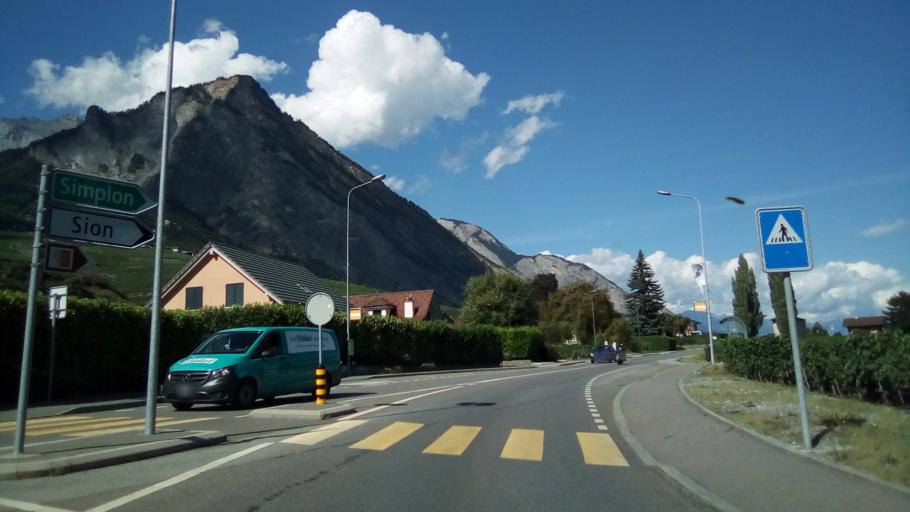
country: CH
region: Valais
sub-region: Martigny District
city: Saillon
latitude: 46.1763
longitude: 7.1920
